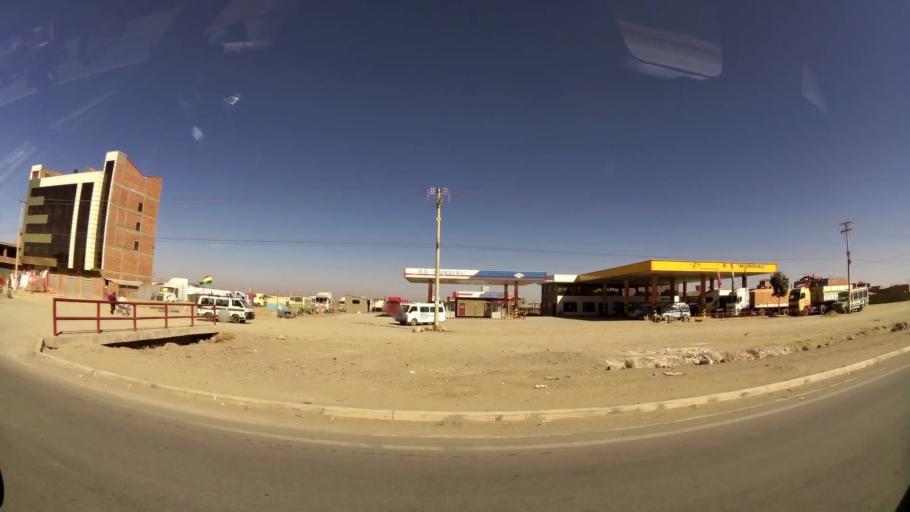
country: BO
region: La Paz
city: La Paz
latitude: -16.6147
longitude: -68.1814
